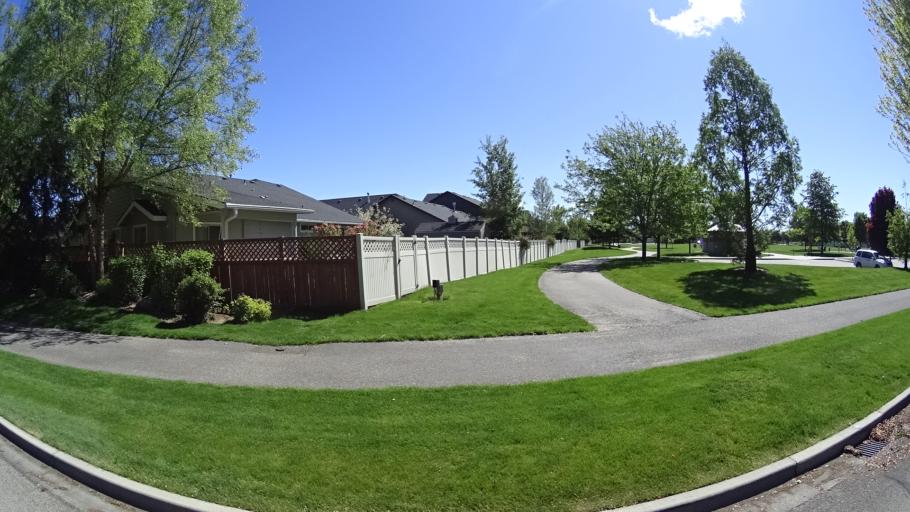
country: US
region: Idaho
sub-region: Ada County
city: Meridian
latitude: 43.6363
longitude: -116.3643
